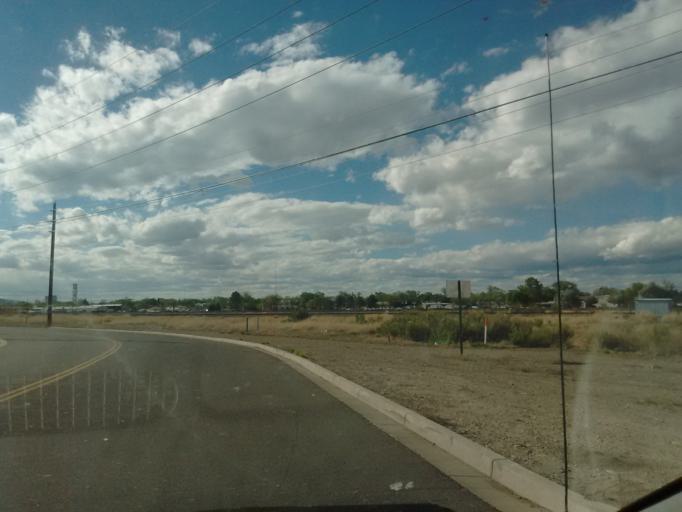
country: US
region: Colorado
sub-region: Mesa County
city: Grand Junction
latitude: 39.0628
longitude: -108.5452
